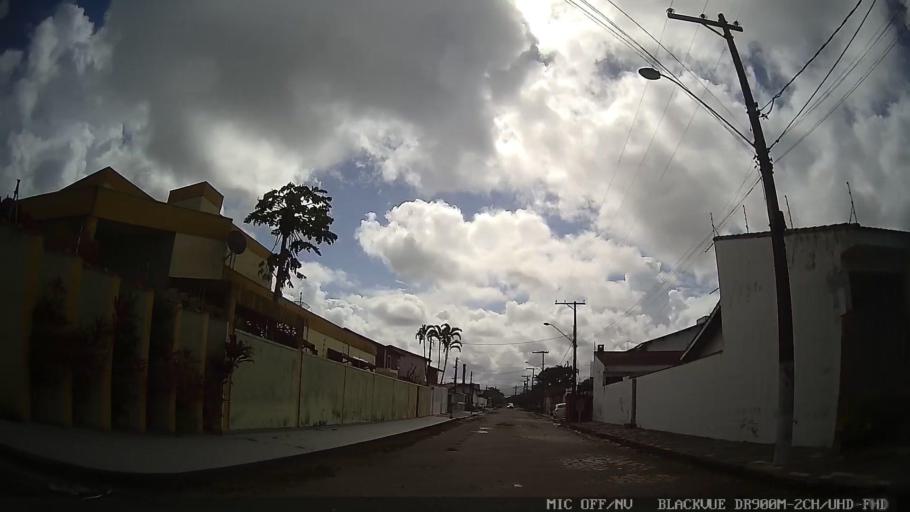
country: BR
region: Sao Paulo
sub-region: Itanhaem
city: Itanhaem
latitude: -24.2035
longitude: -46.8249
